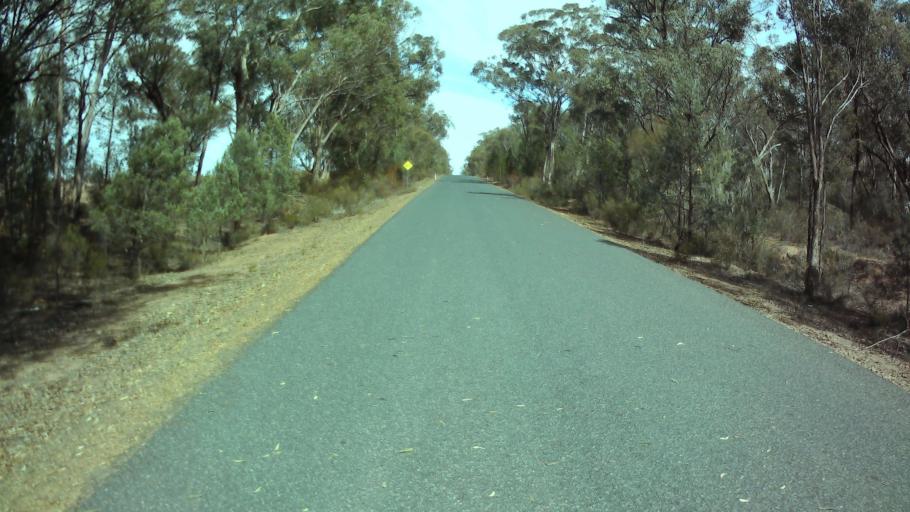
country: AU
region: New South Wales
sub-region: Weddin
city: Grenfell
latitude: -33.8068
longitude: 148.0498
